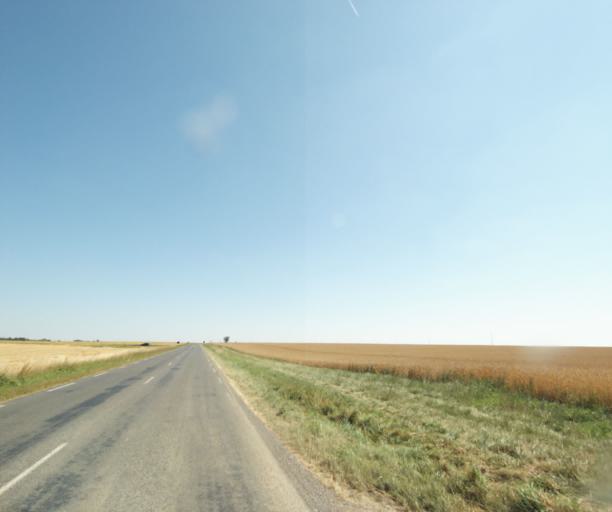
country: FR
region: Ile-de-France
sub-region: Departement de Seine-et-Marne
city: La Chapelle-la-Reine
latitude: 48.2905
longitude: 2.5777
